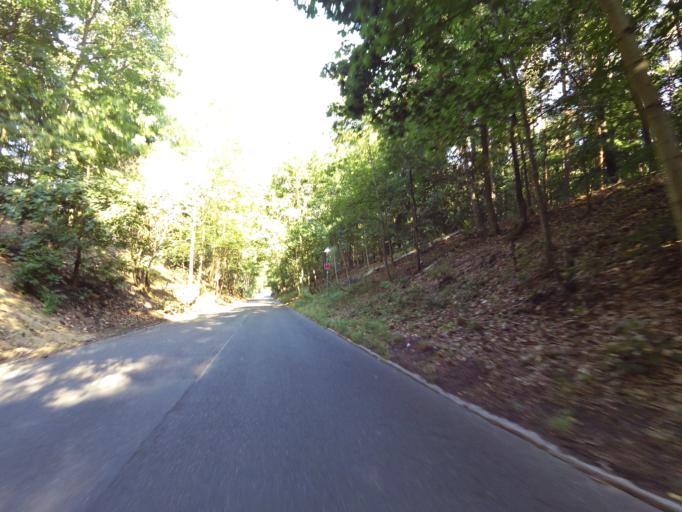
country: DE
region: Berlin
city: Nikolassee
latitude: 52.4442
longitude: 13.1791
